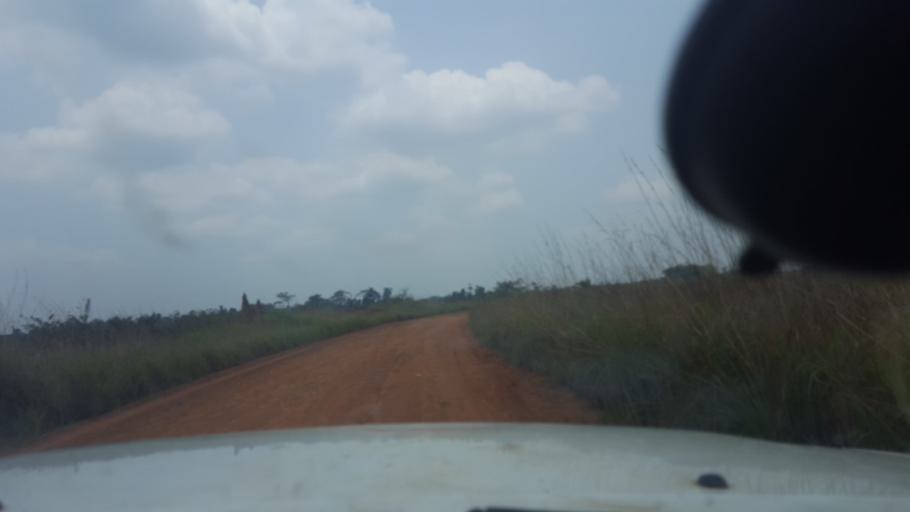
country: CD
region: Bandundu
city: Bandundu
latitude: -3.3304
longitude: 17.2884
